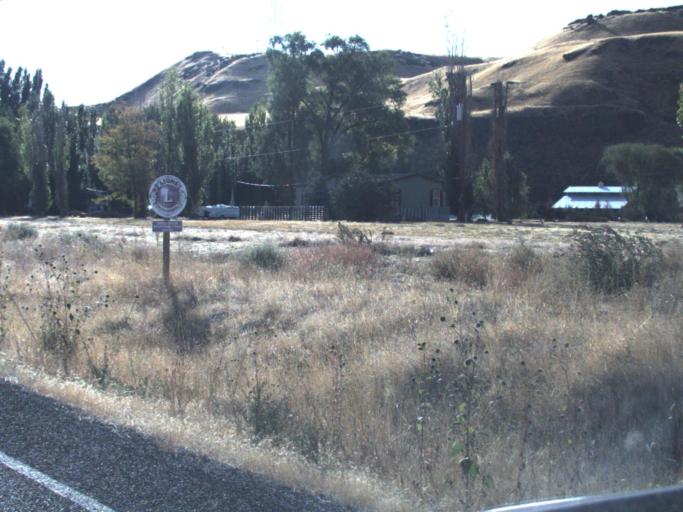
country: US
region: Washington
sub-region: Franklin County
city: Connell
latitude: 46.6434
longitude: -118.5669
